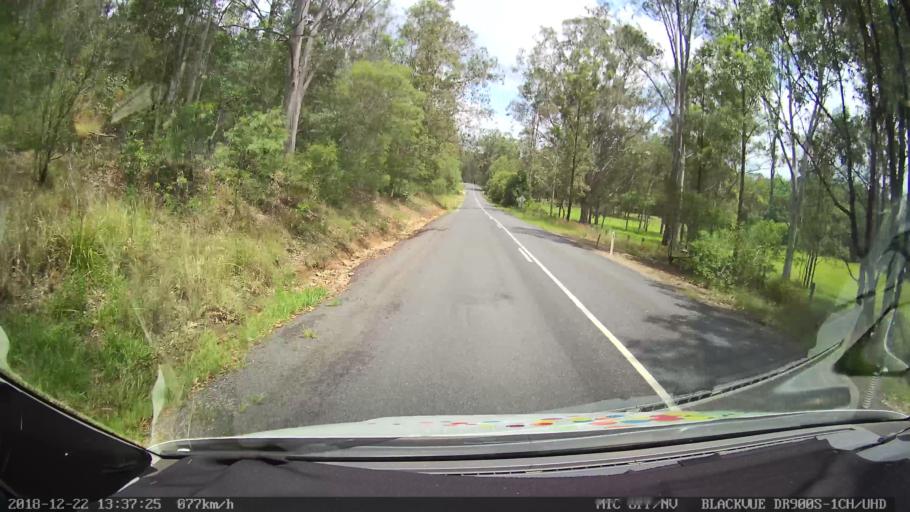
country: AU
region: New South Wales
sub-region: Clarence Valley
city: Coutts Crossing
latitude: -29.8896
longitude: 152.7878
